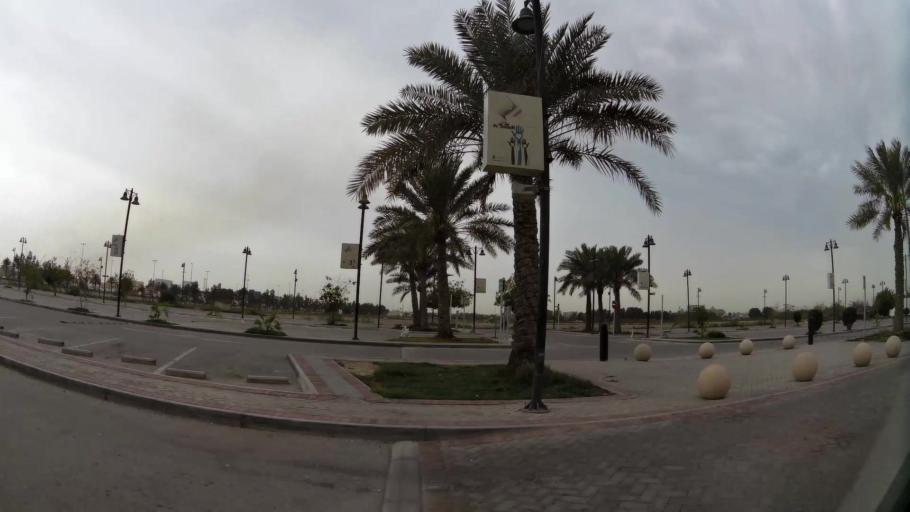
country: BH
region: Manama
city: Jidd Hafs
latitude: 26.1976
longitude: 50.5437
